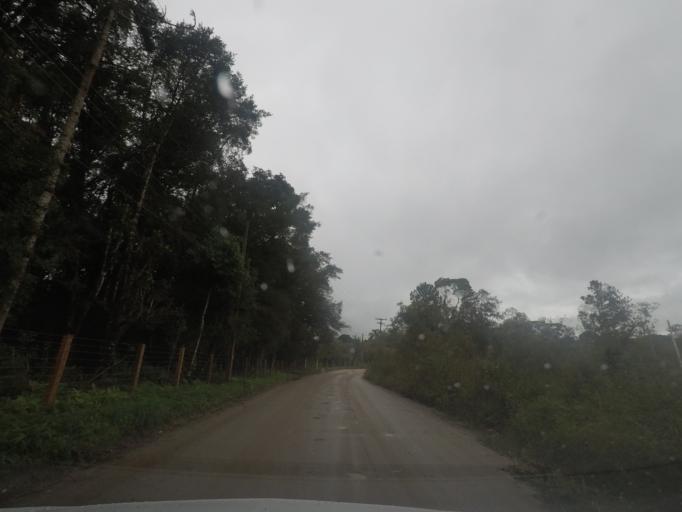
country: BR
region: Parana
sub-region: Campina Grande Do Sul
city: Campina Grande do Sul
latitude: -25.3059
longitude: -49.1091
